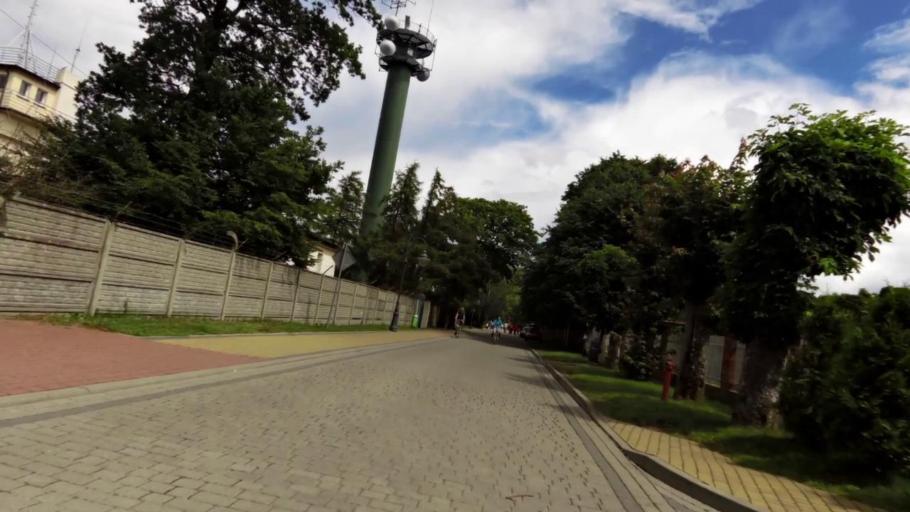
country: PL
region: West Pomeranian Voivodeship
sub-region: Powiat slawienski
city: Darlowo
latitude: 54.5400
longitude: 16.5318
